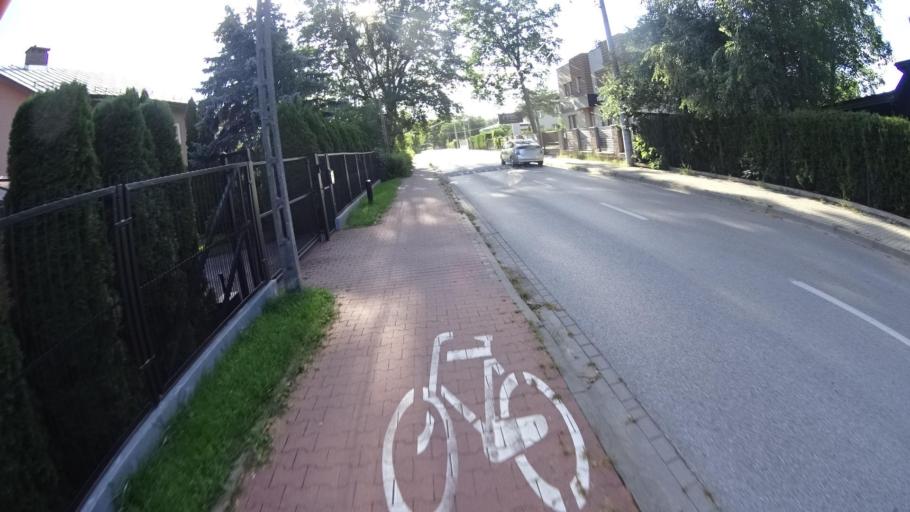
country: PL
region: Masovian Voivodeship
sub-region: Powiat piaseczynski
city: Piaseczno
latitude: 52.0642
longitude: 21.0066
